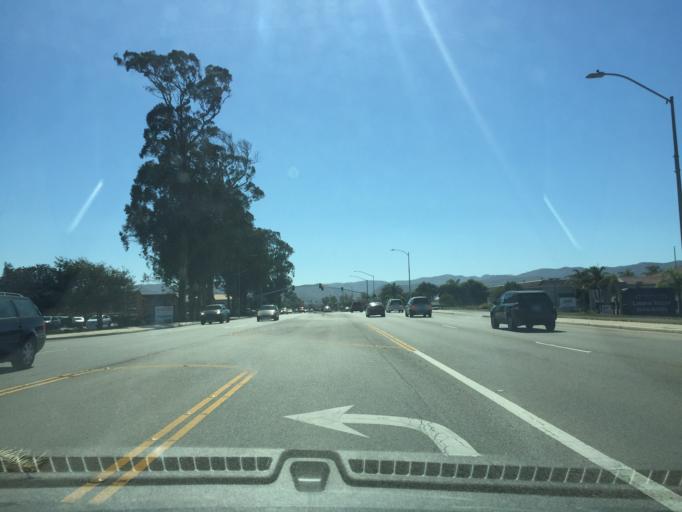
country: US
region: California
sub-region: Santa Barbara County
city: Lompoc
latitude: 34.6643
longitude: -120.4577
